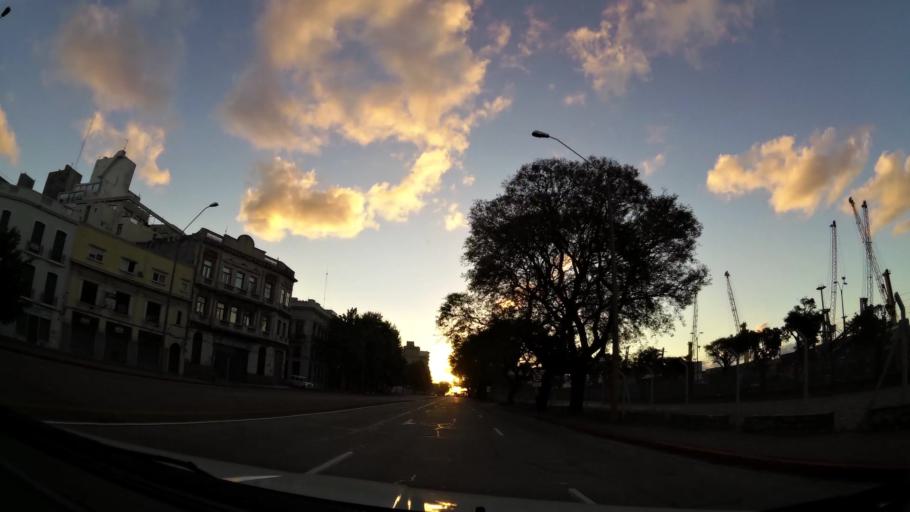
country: UY
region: Montevideo
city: Montevideo
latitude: -34.9036
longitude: -56.2072
